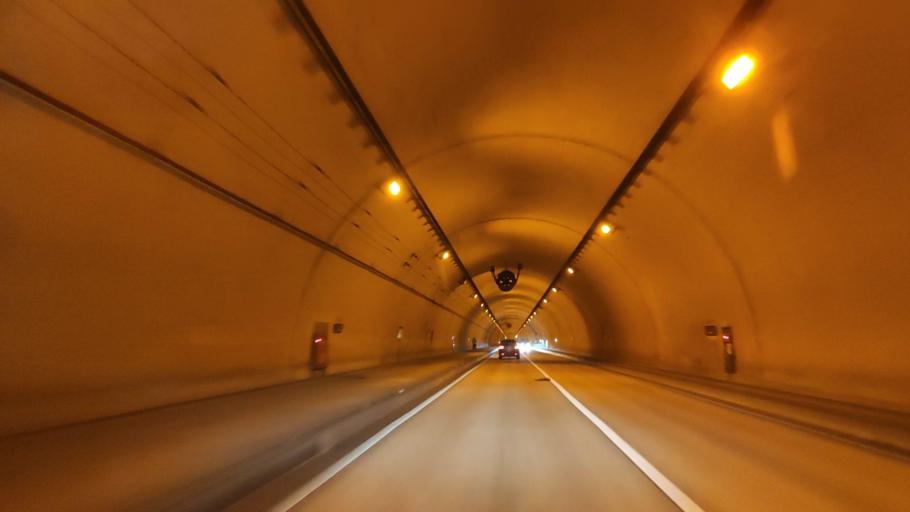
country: JP
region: Ehime
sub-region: Shikoku-chuo Shi
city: Matsuyama
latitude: 33.8776
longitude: 132.7133
